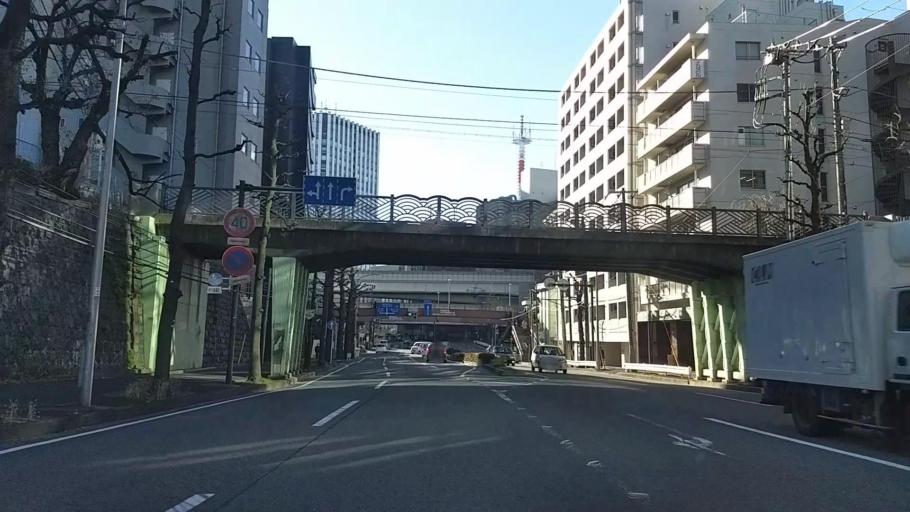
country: JP
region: Kanagawa
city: Yokohama
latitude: 35.4700
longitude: 139.6188
